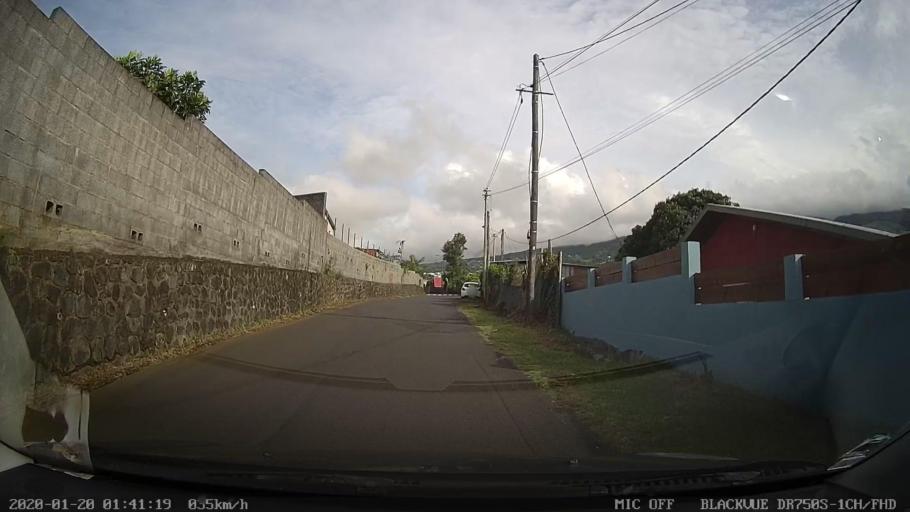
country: RE
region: Reunion
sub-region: Reunion
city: Sainte-Marie
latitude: -20.9248
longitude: 55.5175
